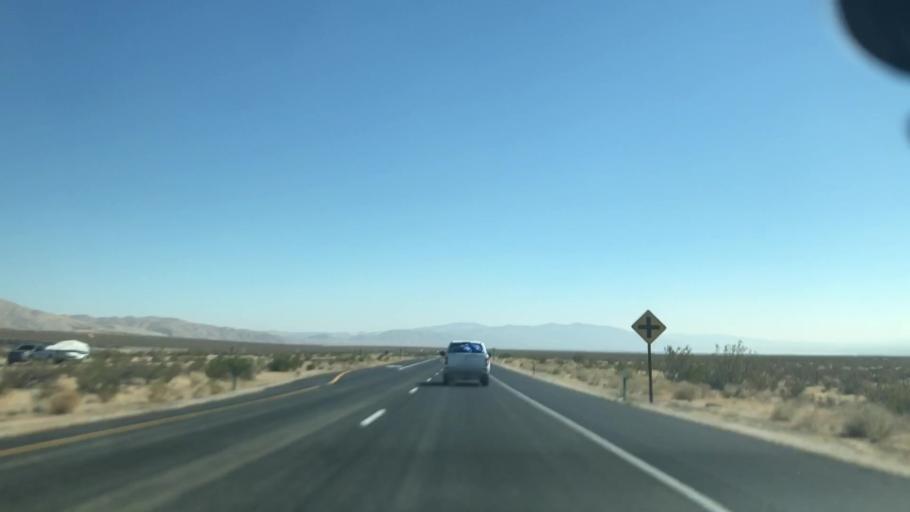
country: US
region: California
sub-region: Kern County
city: California City
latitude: 35.2059
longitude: -118.0607
